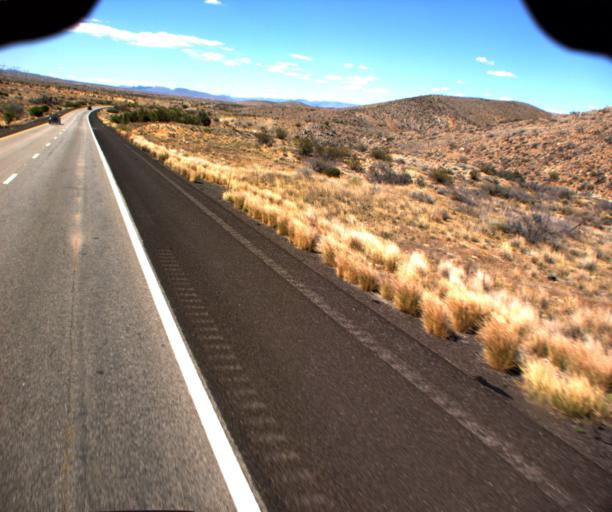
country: US
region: Arizona
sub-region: Mohave County
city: Kingman
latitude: 34.9614
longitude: -113.6697
